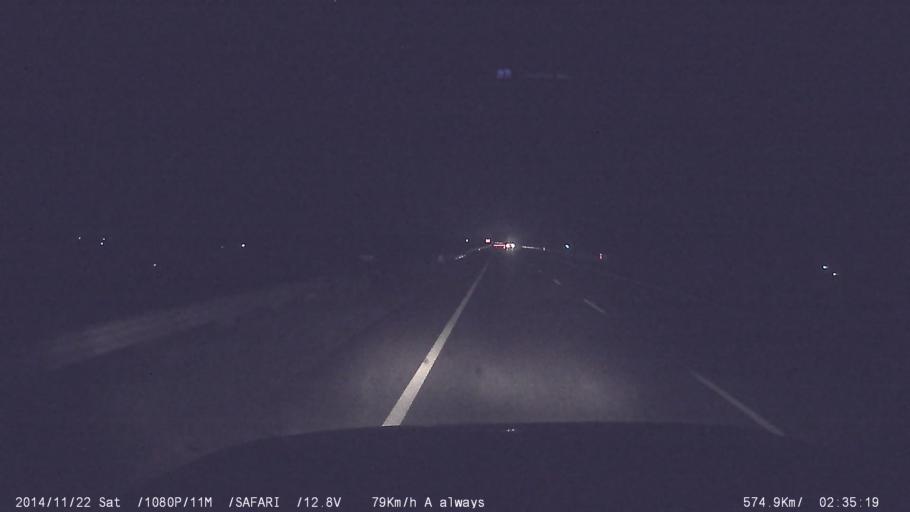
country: IN
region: Tamil Nadu
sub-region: Salem
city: Belur
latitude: 11.6518
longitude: 78.3885
